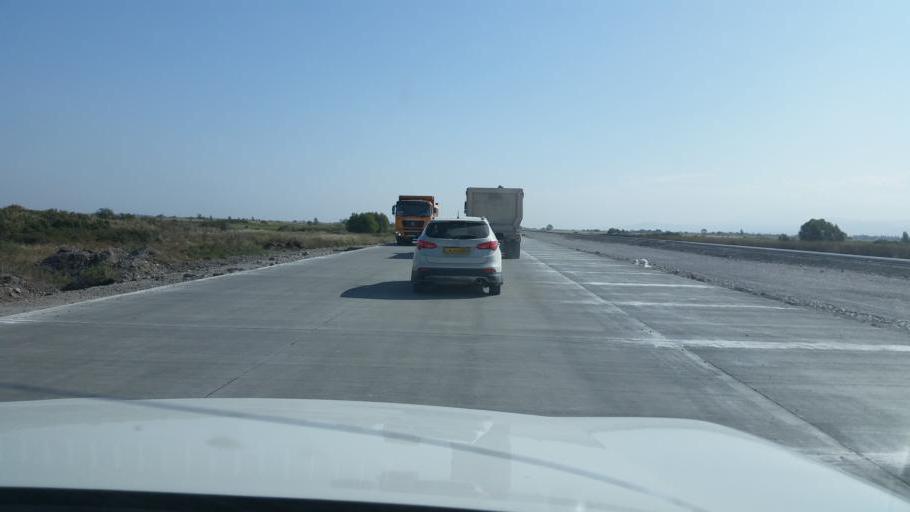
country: KZ
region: Almaty Oblysy
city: Turgen'
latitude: 43.5312
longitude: 77.6013
